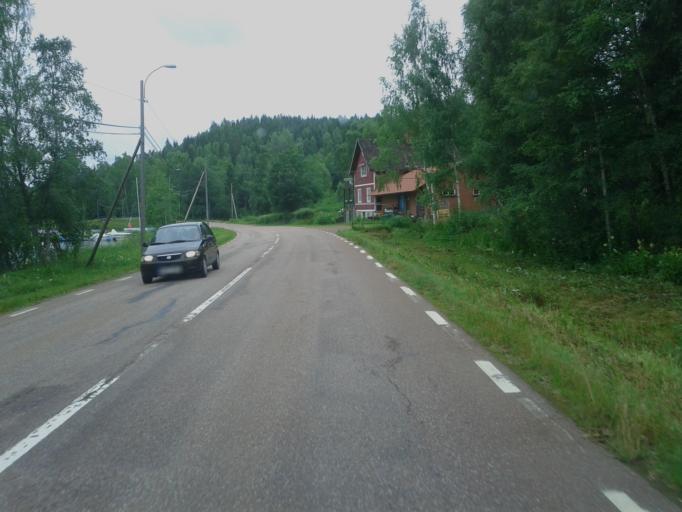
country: SE
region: Dalarna
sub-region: Smedjebackens Kommun
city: Smedjebacken
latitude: 60.3134
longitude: 15.3742
